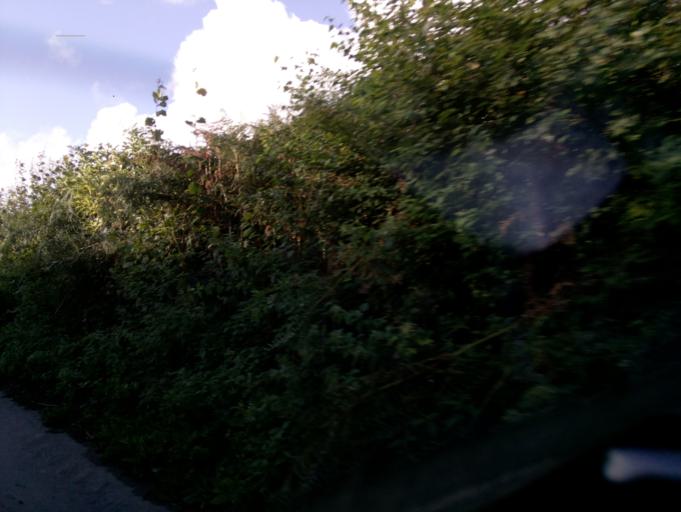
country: GB
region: England
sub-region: Devon
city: Totnes
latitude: 50.3523
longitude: -3.7193
